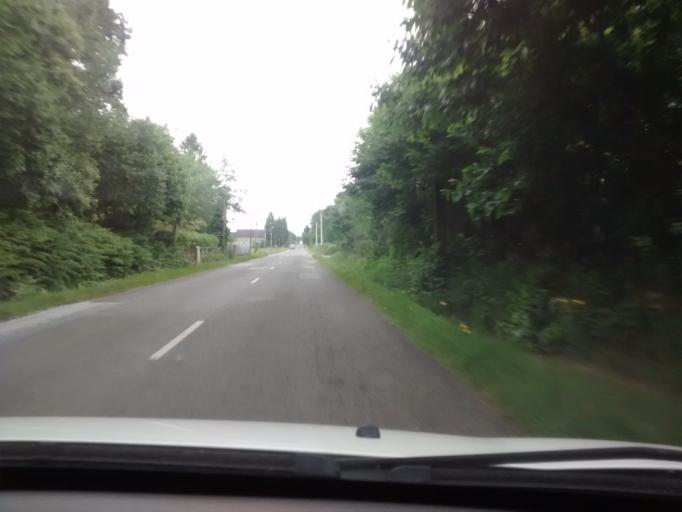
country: FR
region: Brittany
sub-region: Departement d'Ille-et-Vilaine
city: La Bouexiere
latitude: 48.1641
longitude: -1.4394
